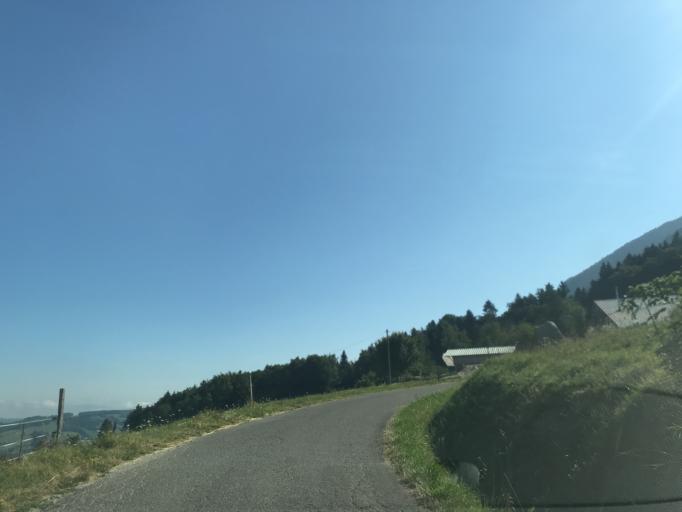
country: FR
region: Rhone-Alpes
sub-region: Departement de la Haute-Savoie
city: Thorens-Glieres
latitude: 45.9708
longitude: 6.2271
